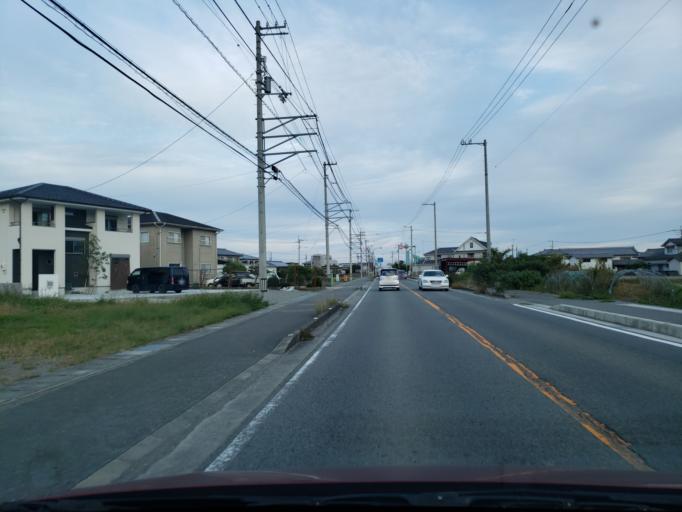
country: JP
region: Tokushima
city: Kamojimacho-jogejima
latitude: 34.1000
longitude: 134.3353
